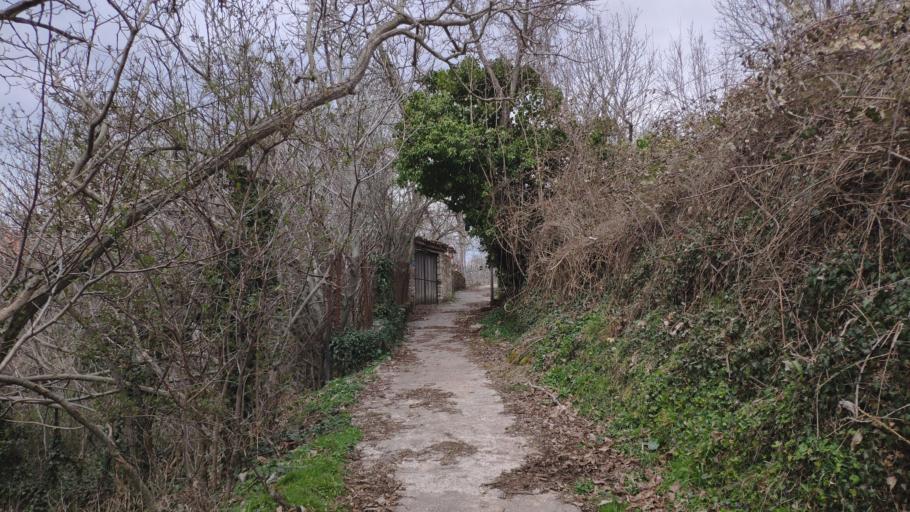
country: GR
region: Central Greece
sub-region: Nomos Fokidos
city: Amfissa
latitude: 38.6425
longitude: 22.4246
